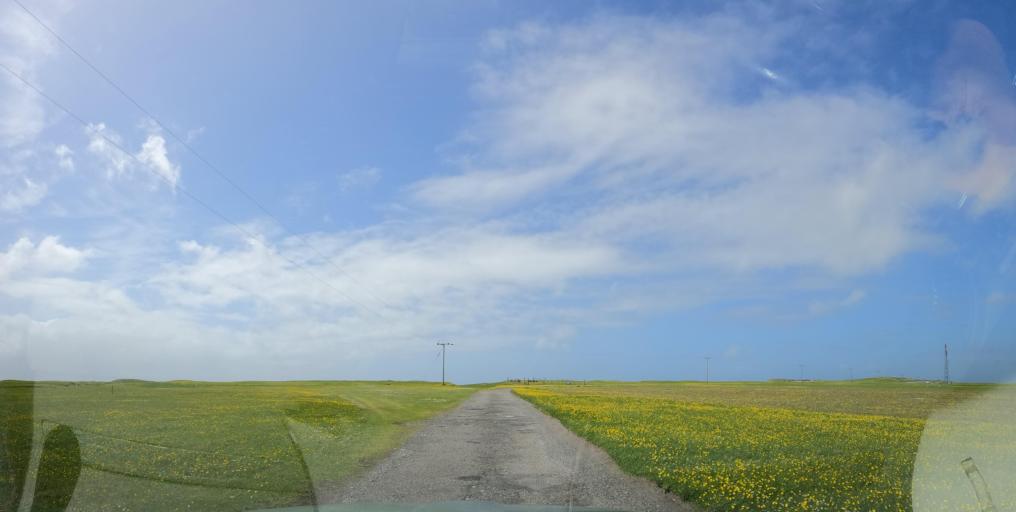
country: GB
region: Scotland
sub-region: Eilean Siar
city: Isle of South Uist
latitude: 57.1646
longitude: -7.3985
